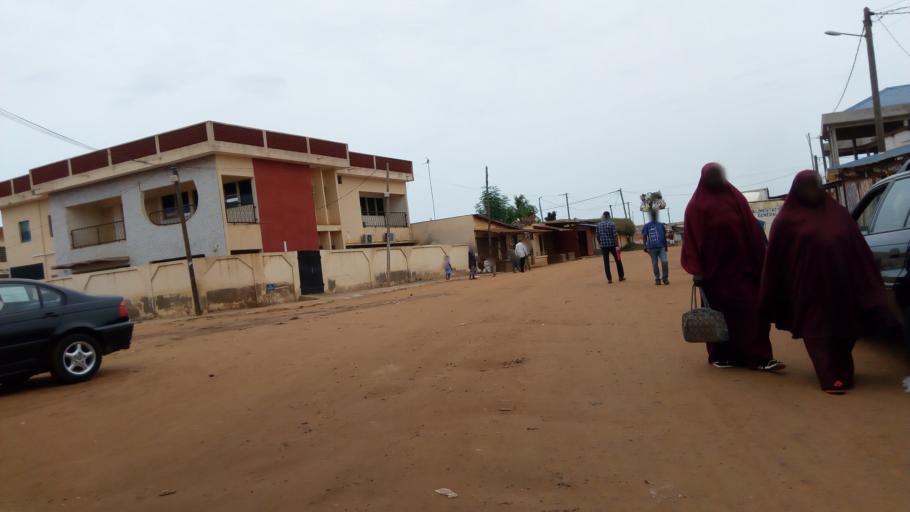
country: TG
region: Maritime
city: Lome
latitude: 6.1602
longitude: 1.2141
